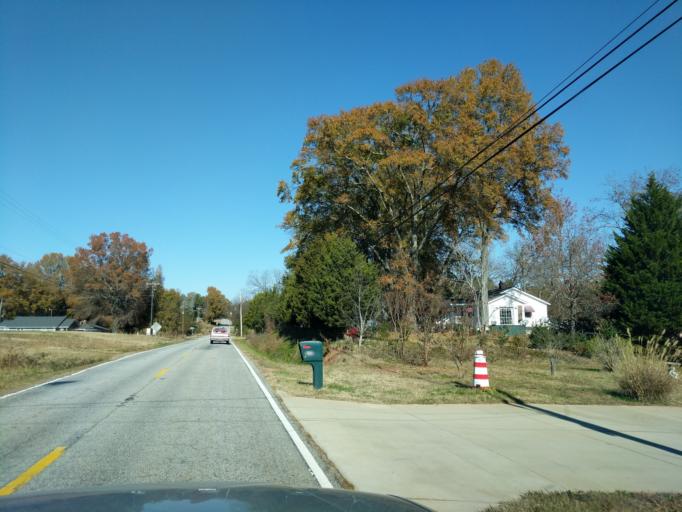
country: US
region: South Carolina
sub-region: Spartanburg County
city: Inman Mills
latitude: 35.0208
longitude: -82.1837
